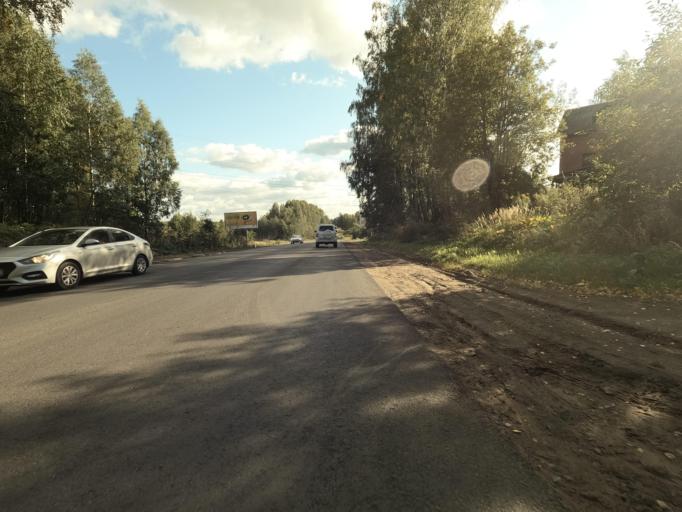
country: RU
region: Leningrad
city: Koltushi
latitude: 59.9321
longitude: 30.6645
